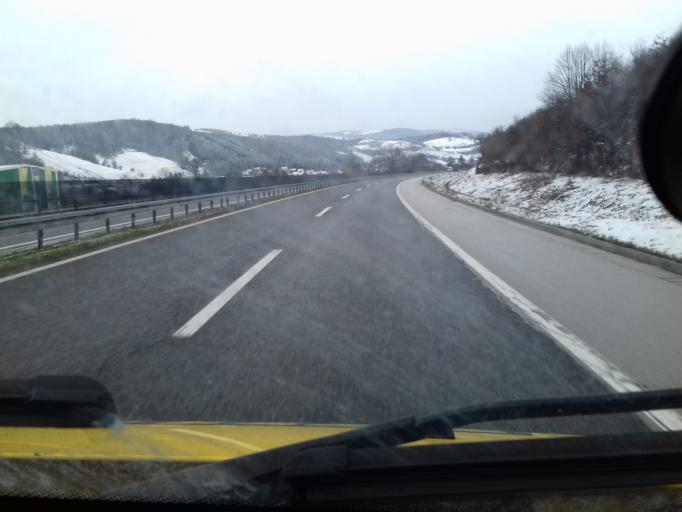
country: BA
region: Federation of Bosnia and Herzegovina
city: Visoko
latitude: 43.9928
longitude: 18.2118
